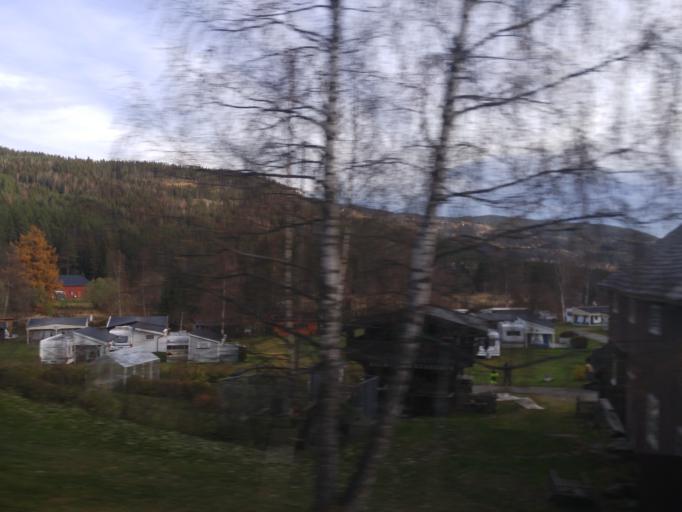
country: NO
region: Oppland
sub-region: Nord-Aurdal
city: Fagernes
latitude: 61.0336
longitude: 9.1765
